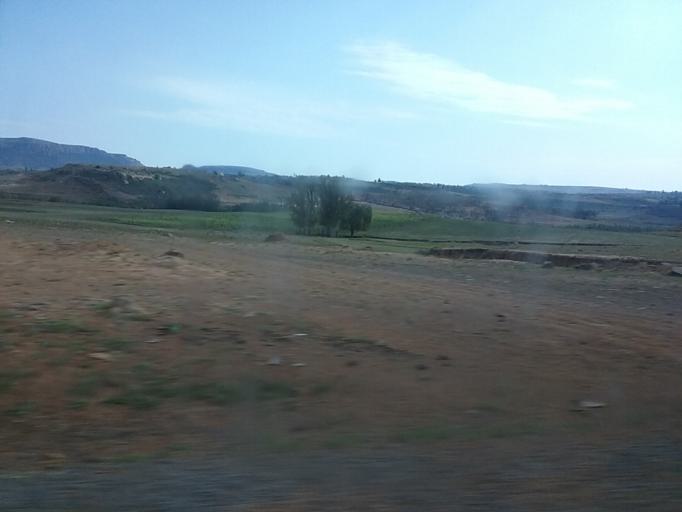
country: LS
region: Berea
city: Teyateyaneng
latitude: -29.0853
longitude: 27.9145
